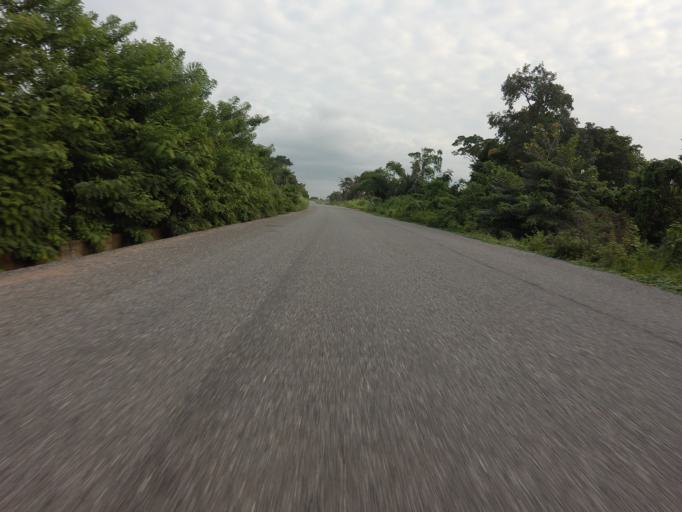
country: GH
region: Volta
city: Kpandu
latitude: 6.8614
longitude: 0.3969
